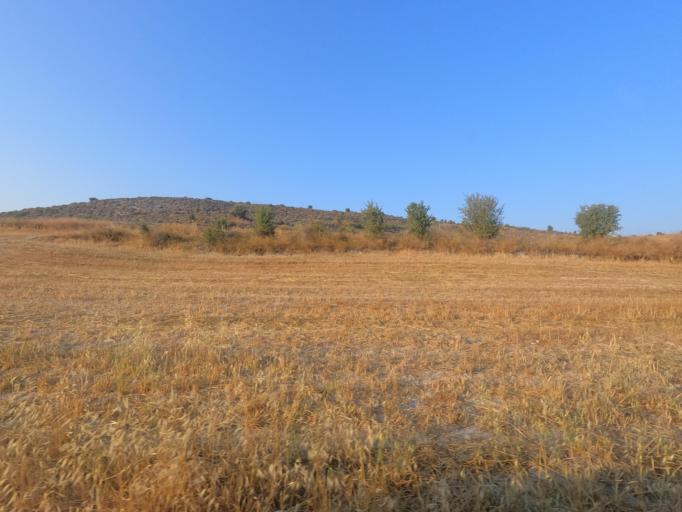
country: CY
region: Larnaka
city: Tersefanou
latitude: 34.9037
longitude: 33.5096
